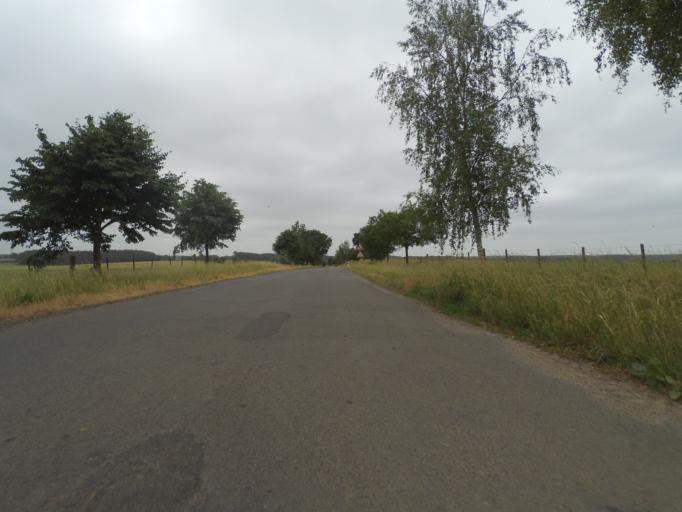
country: DE
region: Mecklenburg-Vorpommern
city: Sternberg
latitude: 53.6645
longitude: 11.8146
